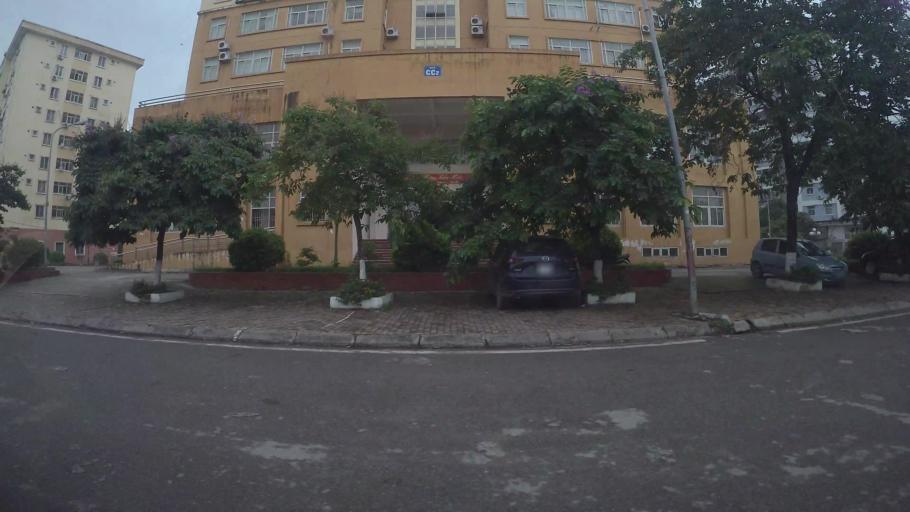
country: VN
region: Ha Noi
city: Van Dien
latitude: 20.9702
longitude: 105.8492
